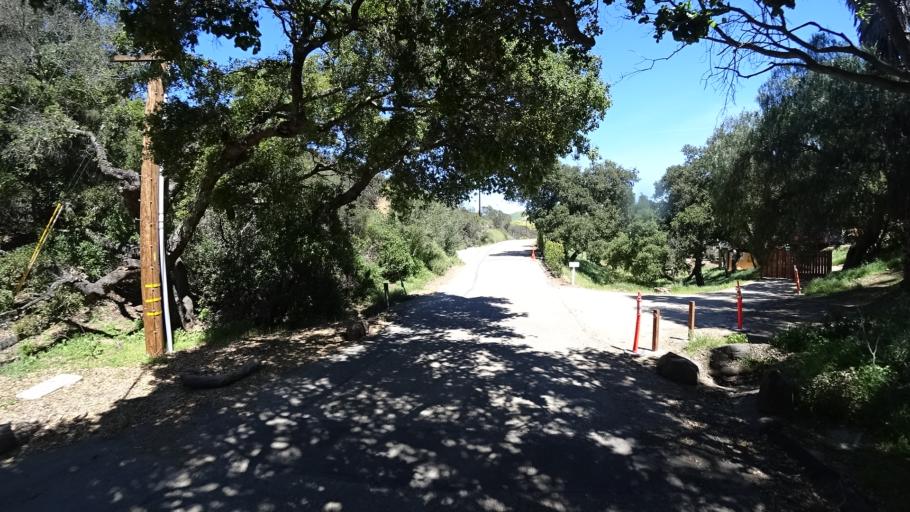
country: US
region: California
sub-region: Ventura County
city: Thousand Oaks
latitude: 34.1657
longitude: -118.8476
